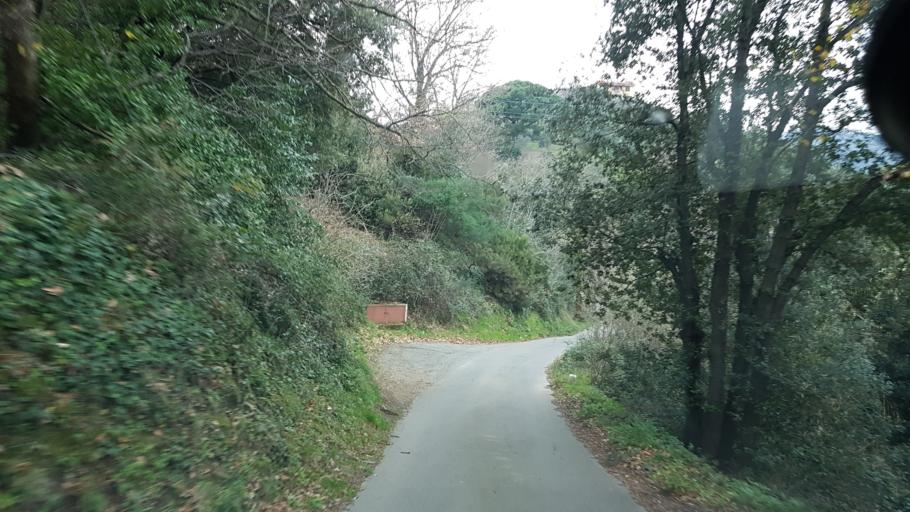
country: IT
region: Liguria
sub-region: Provincia di Savona
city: Valleggia
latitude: 44.3052
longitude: 8.4438
